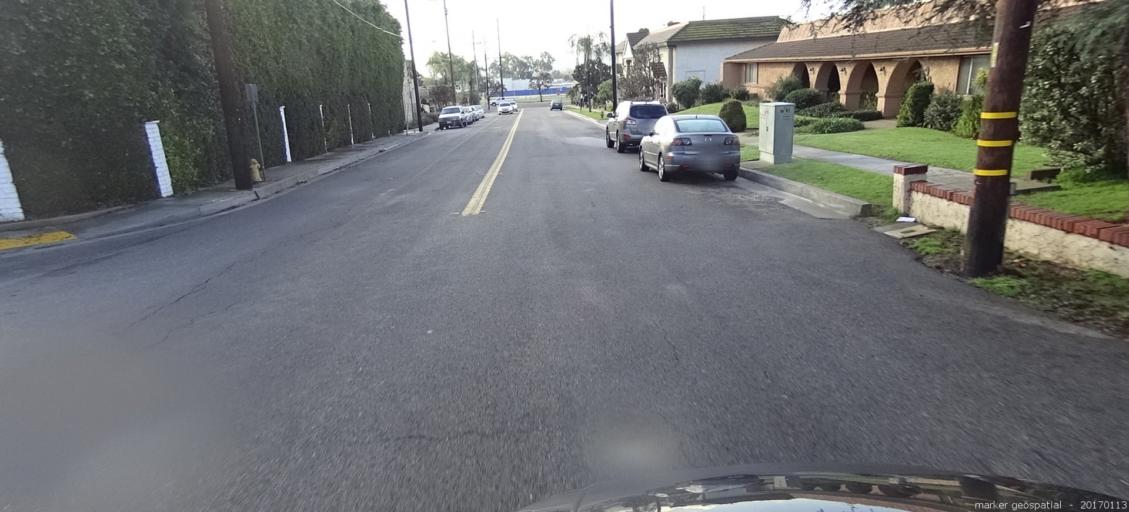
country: US
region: California
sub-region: Orange County
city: La Habra
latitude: 33.9406
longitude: -117.9570
